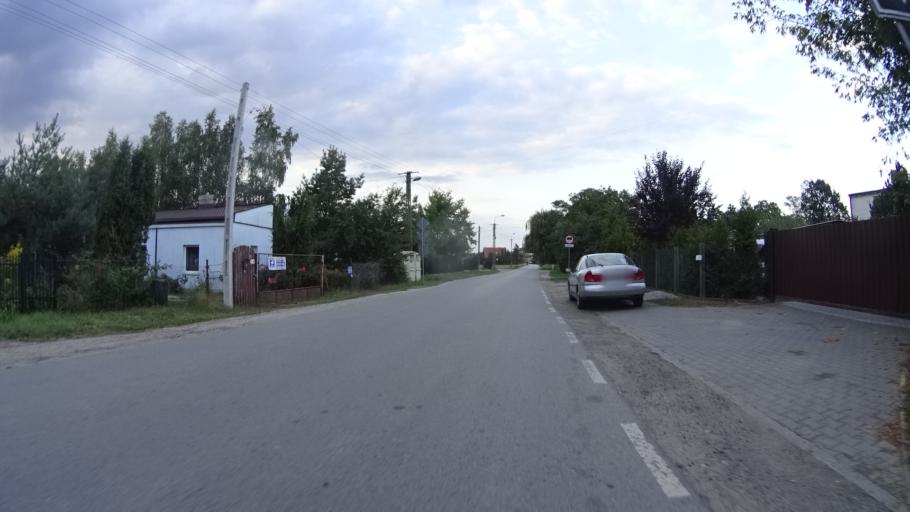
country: PL
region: Masovian Voivodeship
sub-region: Powiat warszawski zachodni
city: Stare Babice
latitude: 52.2316
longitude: 20.8238
